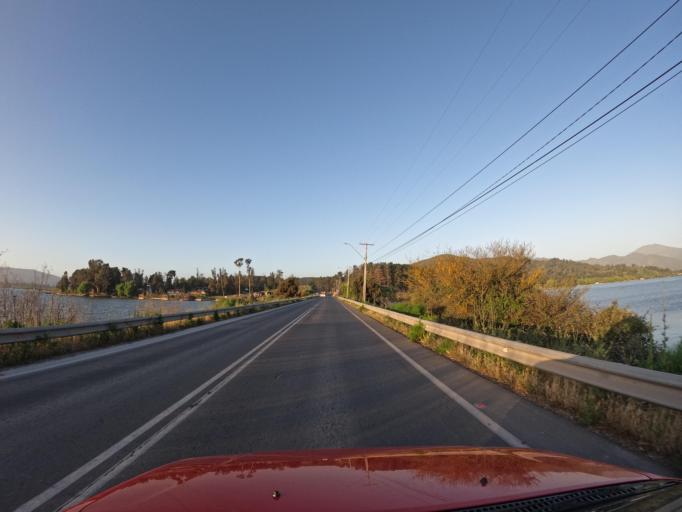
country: CL
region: O'Higgins
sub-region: Provincia de Cachapoal
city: San Vicente
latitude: -34.1479
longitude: -71.3819
